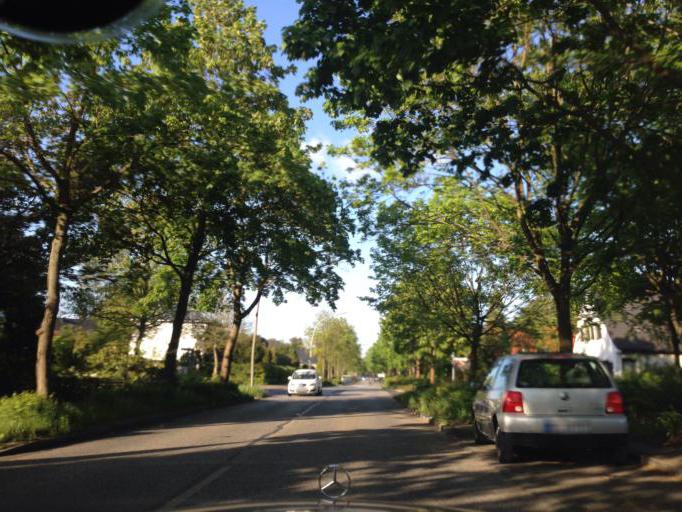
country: DE
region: Hamburg
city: Farmsen-Berne
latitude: 53.6110
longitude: 10.1447
